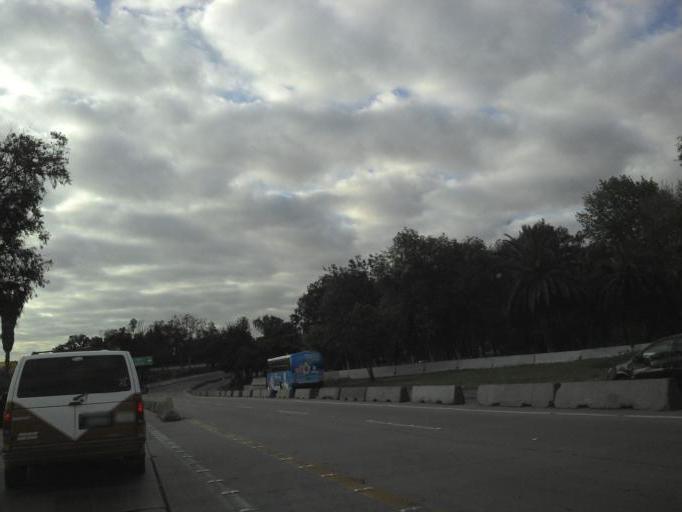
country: MX
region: Baja California
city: Tijuana
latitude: 32.5353
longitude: -117.0289
